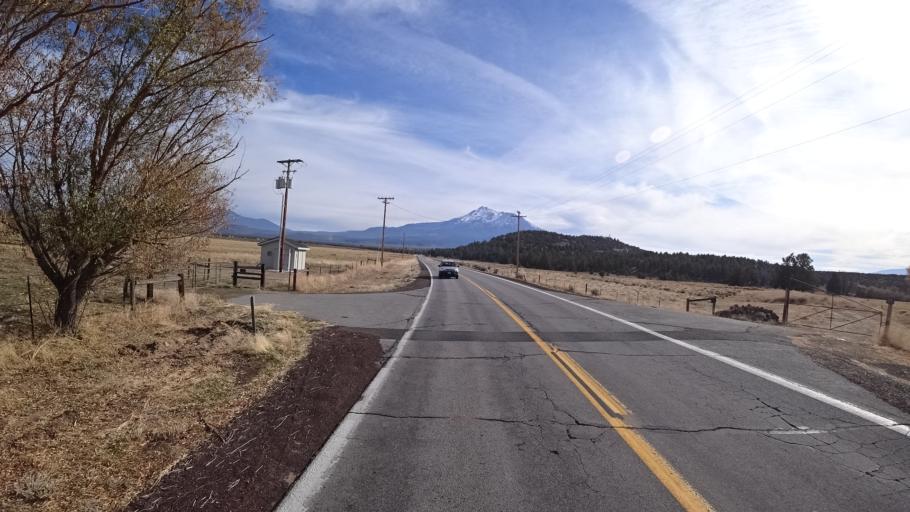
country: US
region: California
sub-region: Siskiyou County
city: Weed
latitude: 41.5454
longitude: -122.3739
